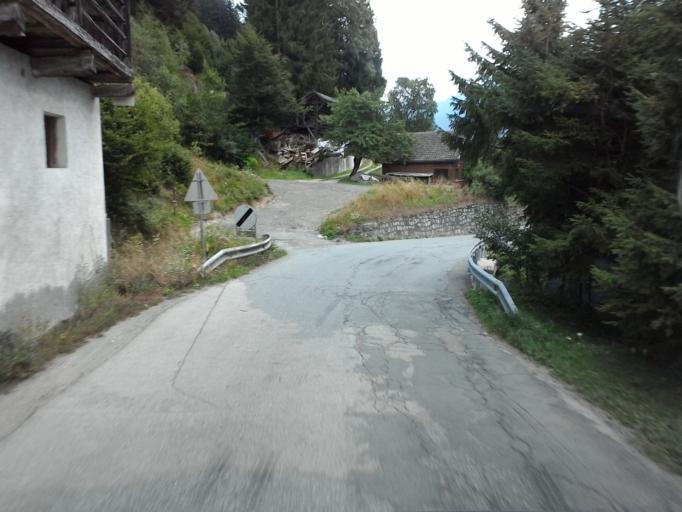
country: AT
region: Carinthia
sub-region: Politischer Bezirk Spittal an der Drau
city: Oberdrauburg
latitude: 46.6760
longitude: 12.9640
